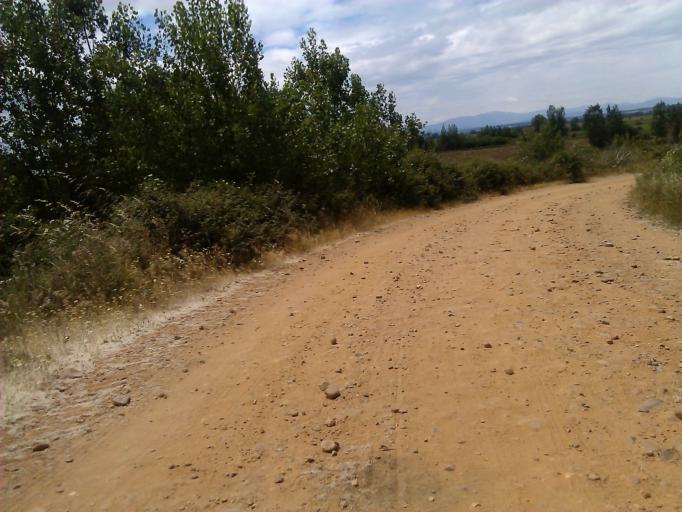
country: ES
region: Castille and Leon
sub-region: Provincia de Leon
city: Bustillo del Paramo
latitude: 42.4595
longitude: -5.7977
